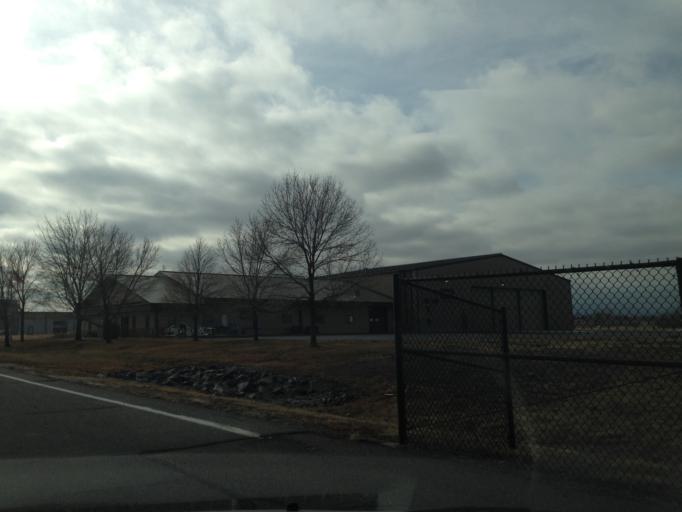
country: US
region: Colorado
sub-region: Boulder County
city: Lafayette
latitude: 40.0076
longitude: -105.0508
